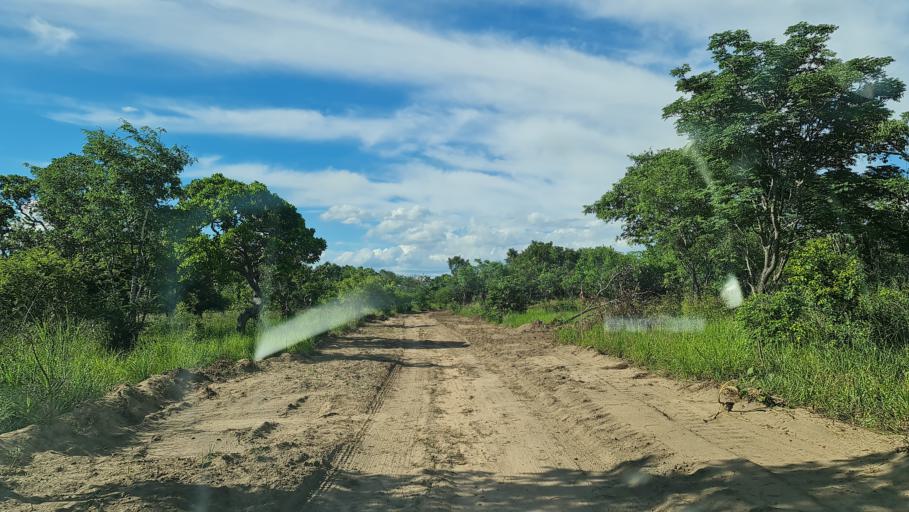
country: MZ
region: Nampula
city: Antonio Enes
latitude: -15.5266
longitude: 40.1269
